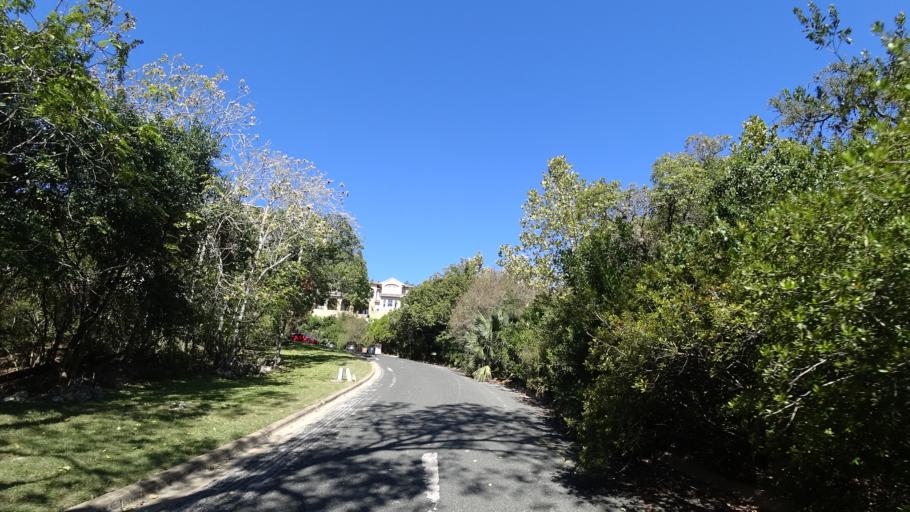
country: US
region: Texas
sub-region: Travis County
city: West Lake Hills
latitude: 30.3518
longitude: -97.7789
